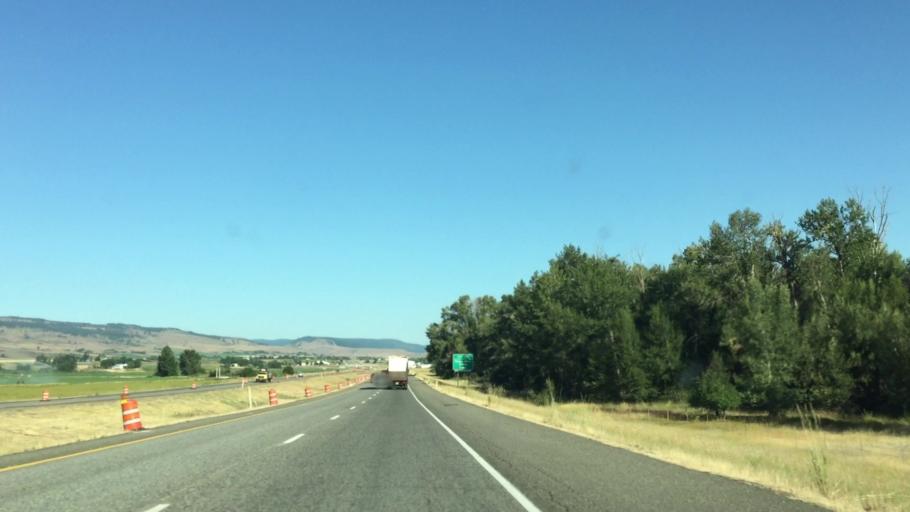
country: US
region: Washington
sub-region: Kittitas County
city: Ellensburg
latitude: 47.0457
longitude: -120.6427
